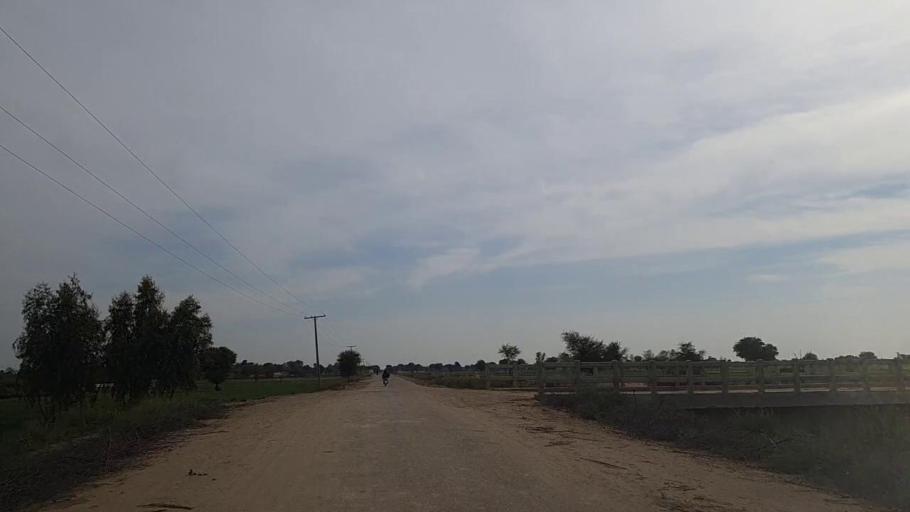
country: PK
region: Sindh
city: Daur
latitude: 26.4226
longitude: 68.4851
